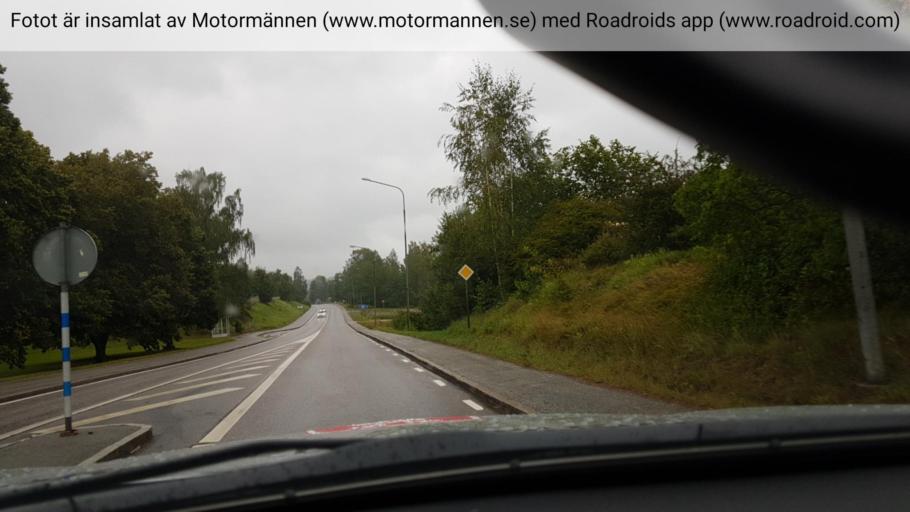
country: SE
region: Vaestra Goetaland
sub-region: Bengtsfors Kommun
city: Billingsfors
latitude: 58.9769
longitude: 12.2460
